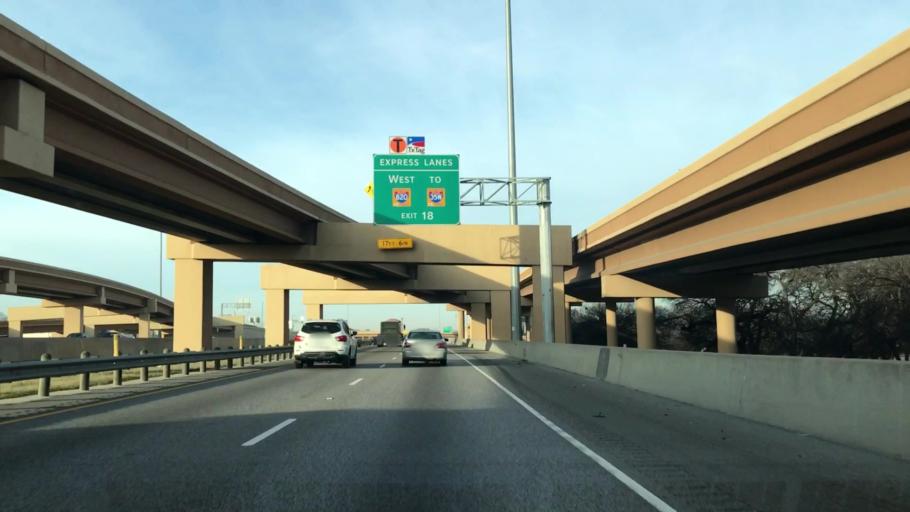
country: US
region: Texas
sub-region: Tarrant County
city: Watauga
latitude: 32.8401
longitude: -97.2592
